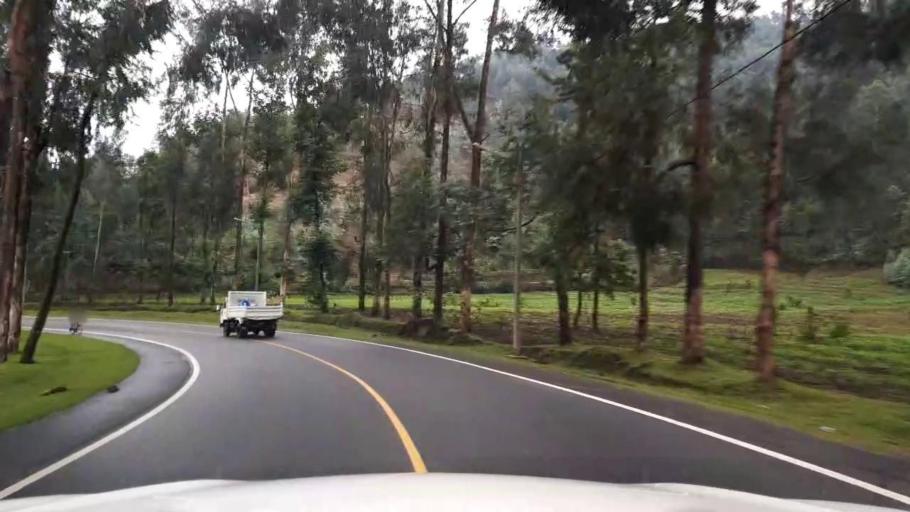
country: RW
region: Northern Province
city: Musanze
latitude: -1.5337
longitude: 29.5690
